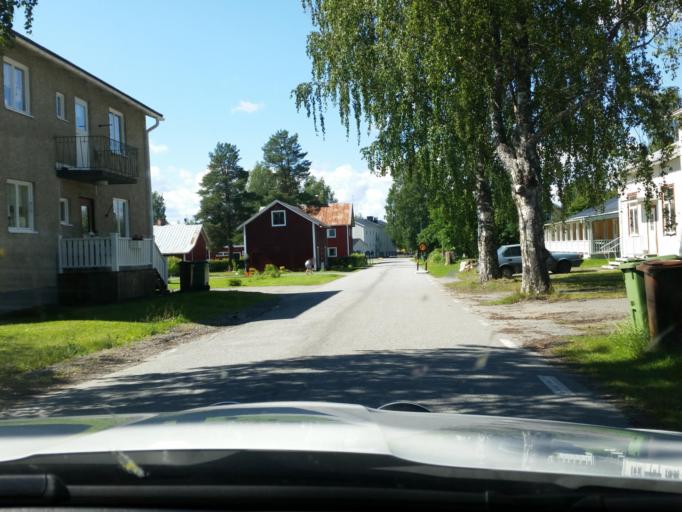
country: SE
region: Norrbotten
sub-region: Alvsbyns Kommun
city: AElvsbyn
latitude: 65.6677
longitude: 20.8694
